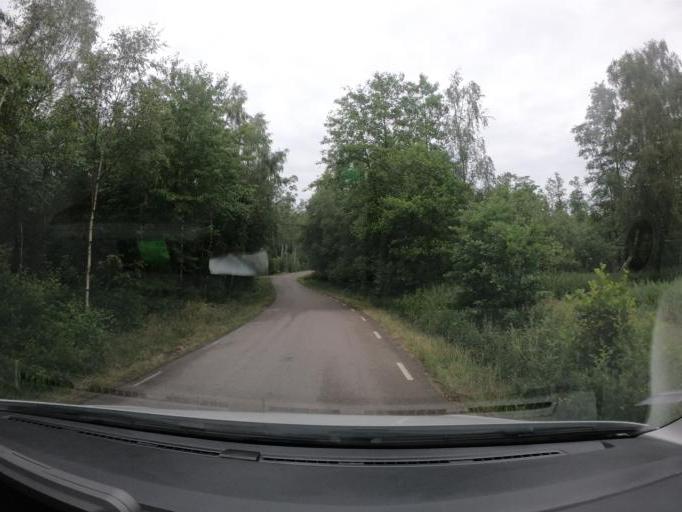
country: SE
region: Skane
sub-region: Orkelljunga Kommun
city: OErkelljunga
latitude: 56.2930
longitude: 13.1208
